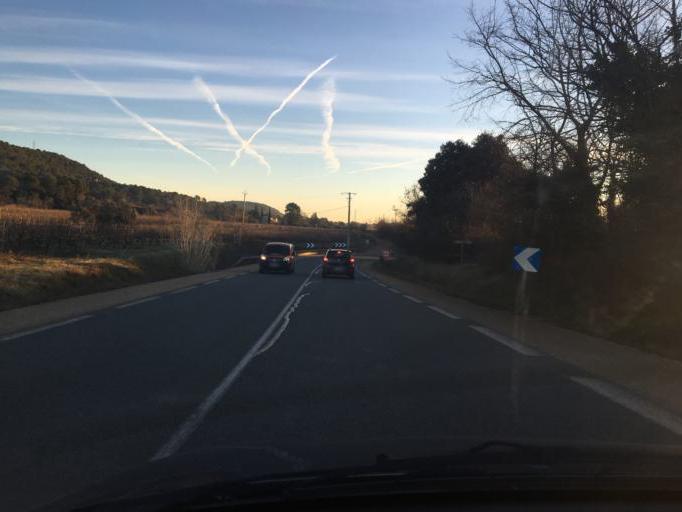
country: FR
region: Provence-Alpes-Cote d'Azur
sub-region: Departement du Var
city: Taradeau
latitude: 43.4495
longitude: 6.4480
